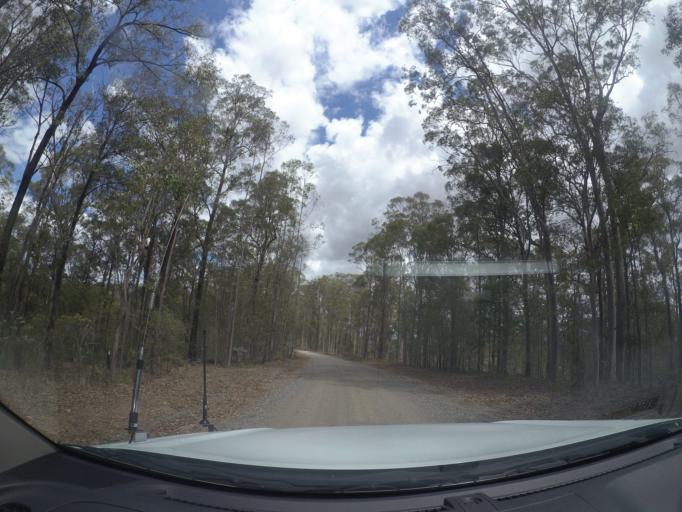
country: AU
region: Queensland
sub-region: Logan
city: Cedar Vale
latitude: -27.9063
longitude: 153.0309
